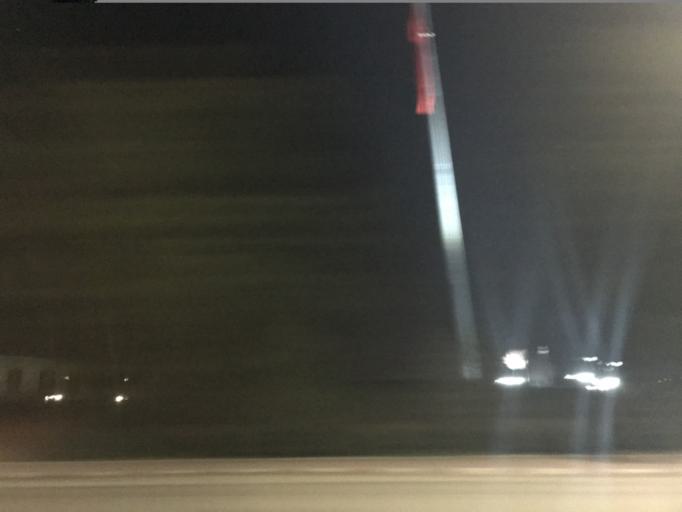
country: TR
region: Karabuk
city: Karabuk
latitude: 41.2072
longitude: 32.6576
